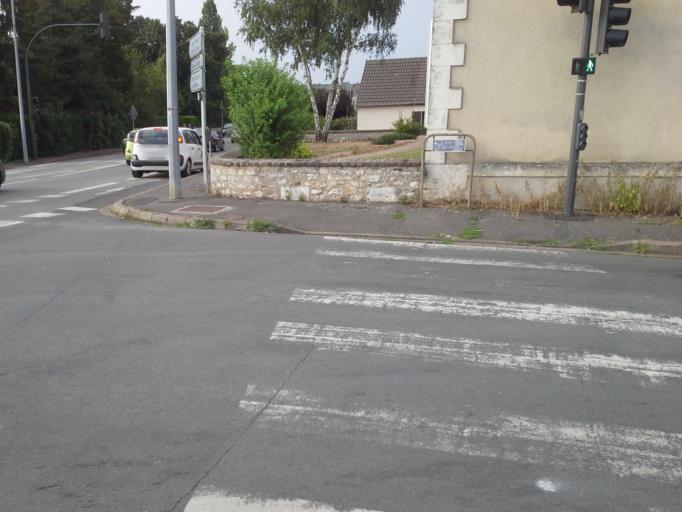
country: FR
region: Centre
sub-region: Departement du Loir-et-Cher
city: Vendome
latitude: 47.8008
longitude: 1.0574
